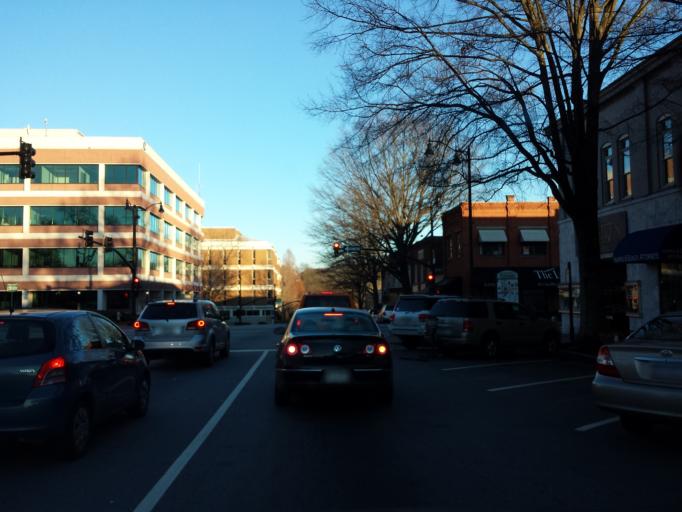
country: US
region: Georgia
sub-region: Cobb County
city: Marietta
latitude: 33.9523
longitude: -84.5495
